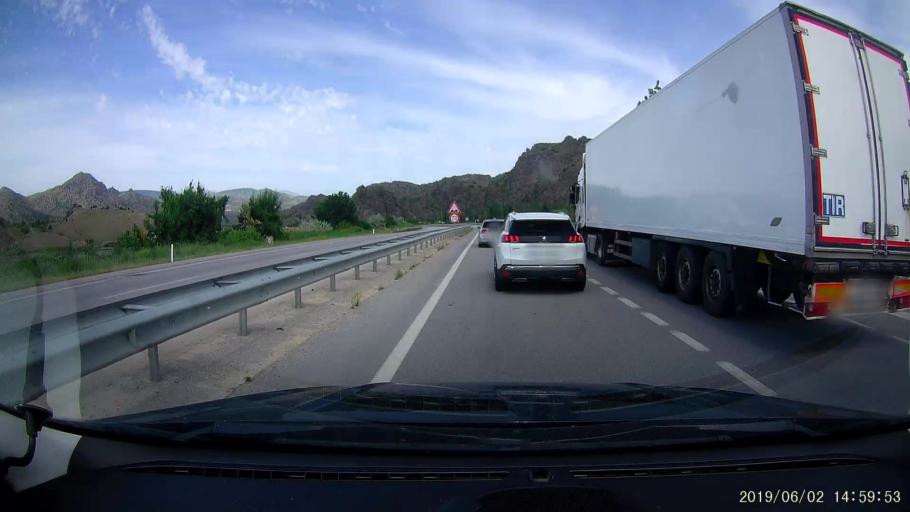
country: TR
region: Corum
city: Osmancik
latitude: 40.9723
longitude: 34.7029
